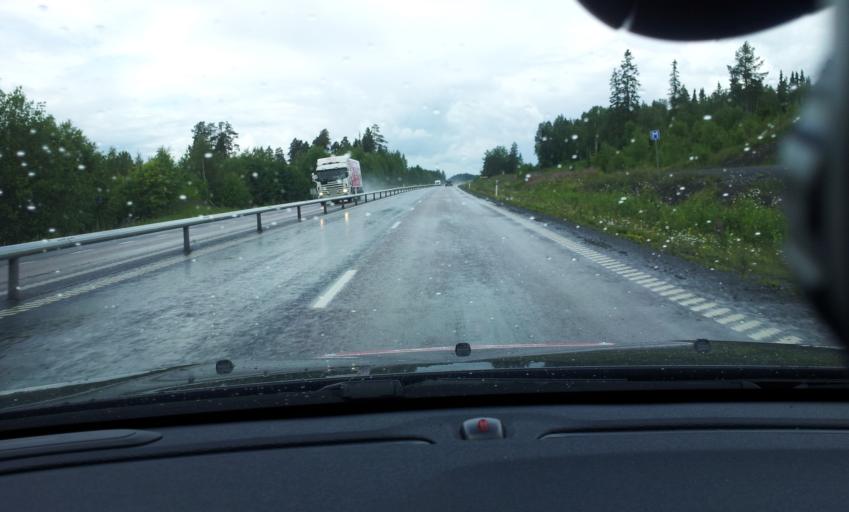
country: SE
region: Jaemtland
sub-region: Krokoms Kommun
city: Krokom
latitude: 63.2957
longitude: 14.5000
